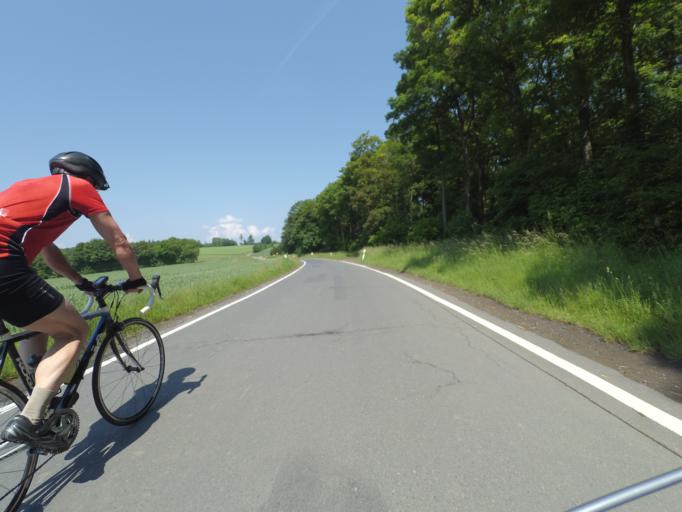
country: DE
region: Rheinland-Pfalz
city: Monreal
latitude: 50.3126
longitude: 7.1891
